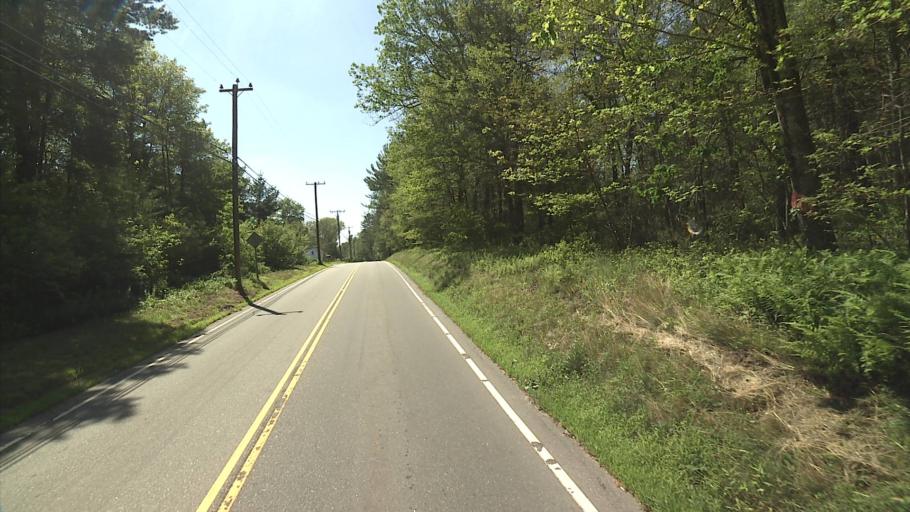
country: US
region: Connecticut
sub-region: Windham County
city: Moosup
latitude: 41.7116
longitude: -71.8438
